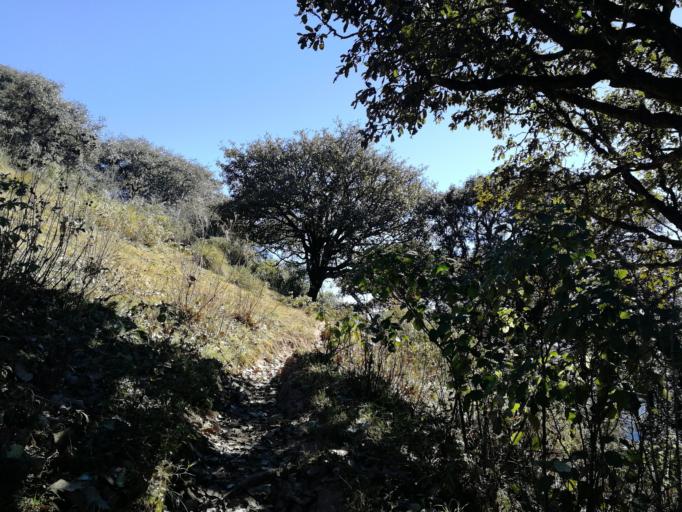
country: MX
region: San Luis Potosi
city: Zaragoza
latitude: 22.0084
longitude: -100.6160
